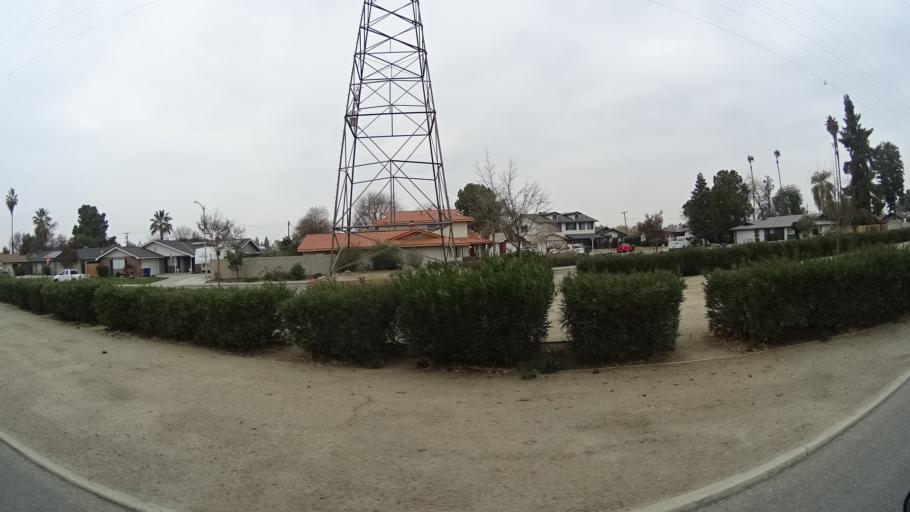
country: US
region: California
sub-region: Kern County
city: Bakersfield
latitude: 35.3878
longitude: -119.0319
